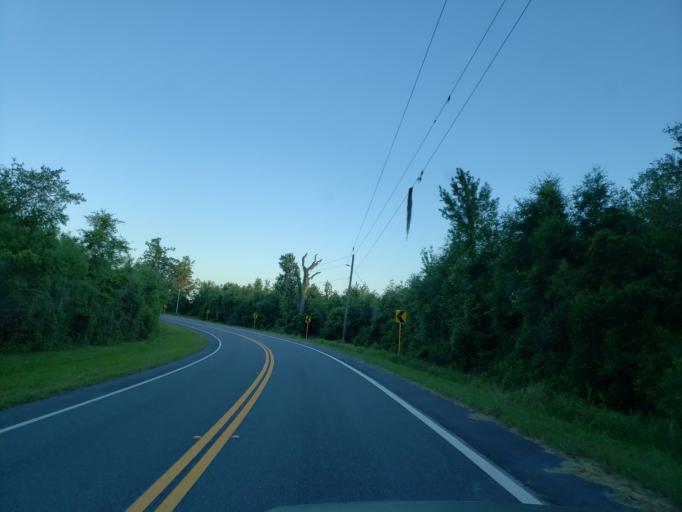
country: US
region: Florida
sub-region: Madison County
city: Madison
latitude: 30.5828
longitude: -83.2411
